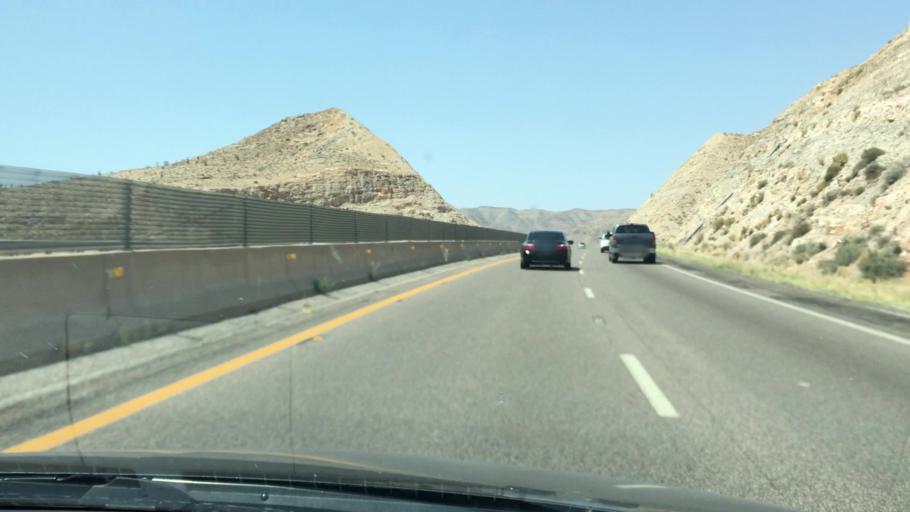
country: US
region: Arizona
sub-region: Mohave County
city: Beaver Dam
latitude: 36.9602
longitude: -113.7648
